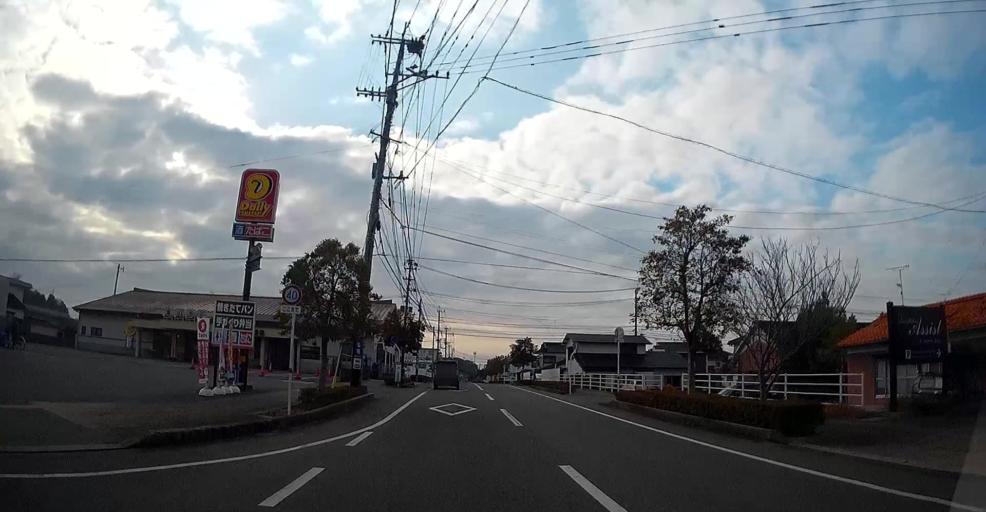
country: JP
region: Kumamoto
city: Hondo
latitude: 32.4446
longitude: 130.2027
